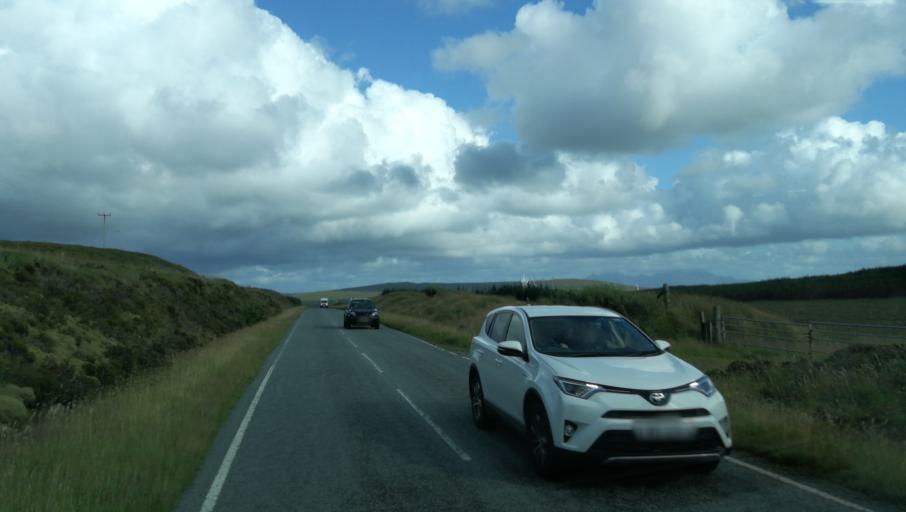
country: GB
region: Scotland
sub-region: Highland
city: Isle of Skye
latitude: 57.4668
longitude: -6.5143
